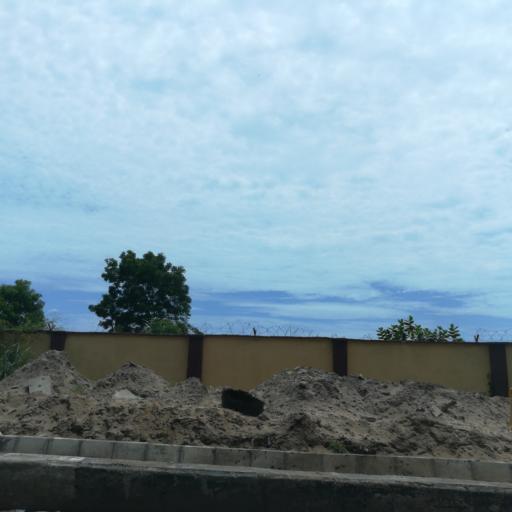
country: NG
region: Lagos
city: Lagos
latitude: 6.4520
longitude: 3.3856
